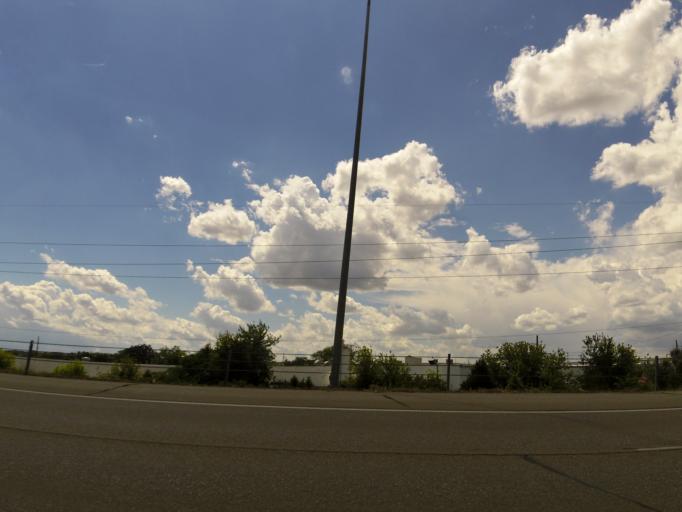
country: US
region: Iowa
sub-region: Linn County
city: Cedar Rapids
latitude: 41.9974
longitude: -91.6671
